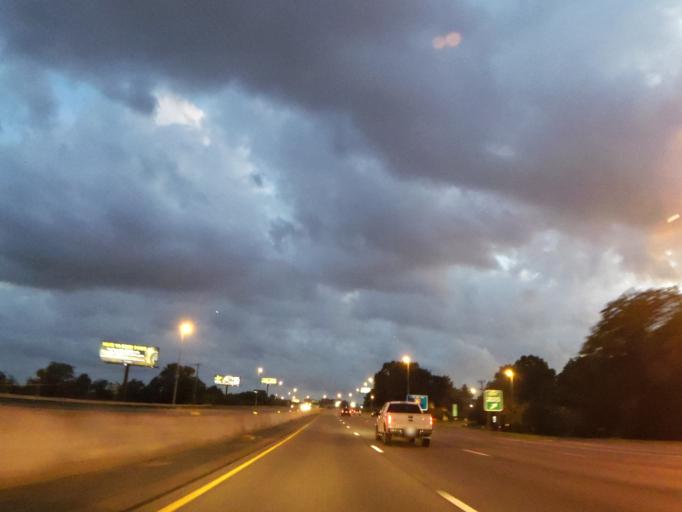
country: US
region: Illinois
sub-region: Saint Clair County
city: Cahokia
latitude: 38.5815
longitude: -90.2244
